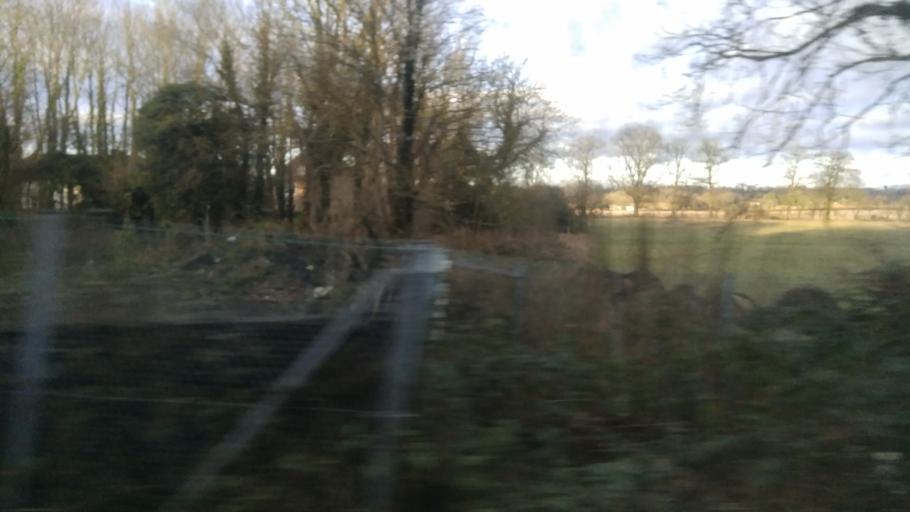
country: GB
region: England
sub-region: Kent
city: Lenham
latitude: 51.1564
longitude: 0.7488
